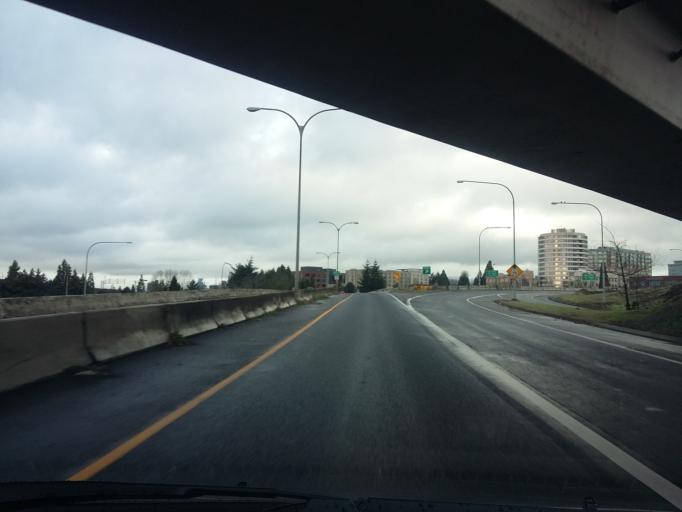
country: US
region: Washington
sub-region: Clark County
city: Vancouver
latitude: 45.6222
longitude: -122.6694
